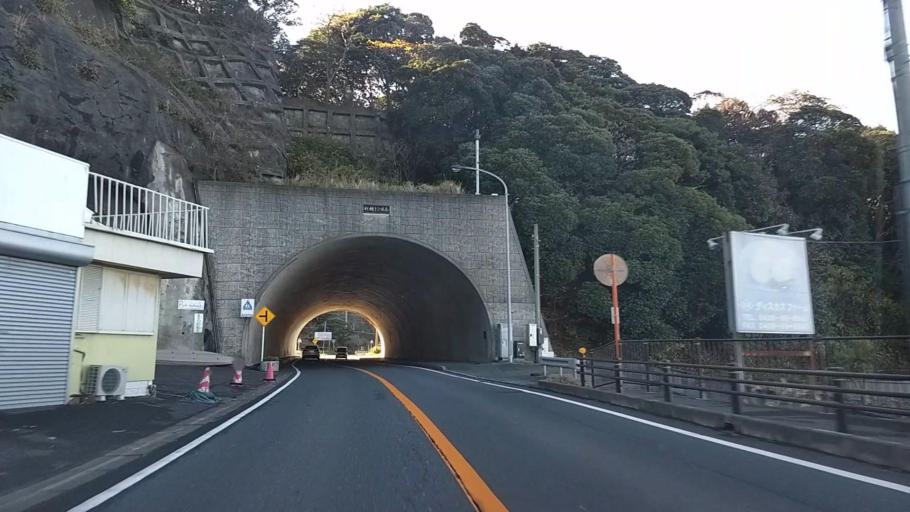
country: JP
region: Chiba
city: Futtsu
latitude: 35.1945
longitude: 139.8233
